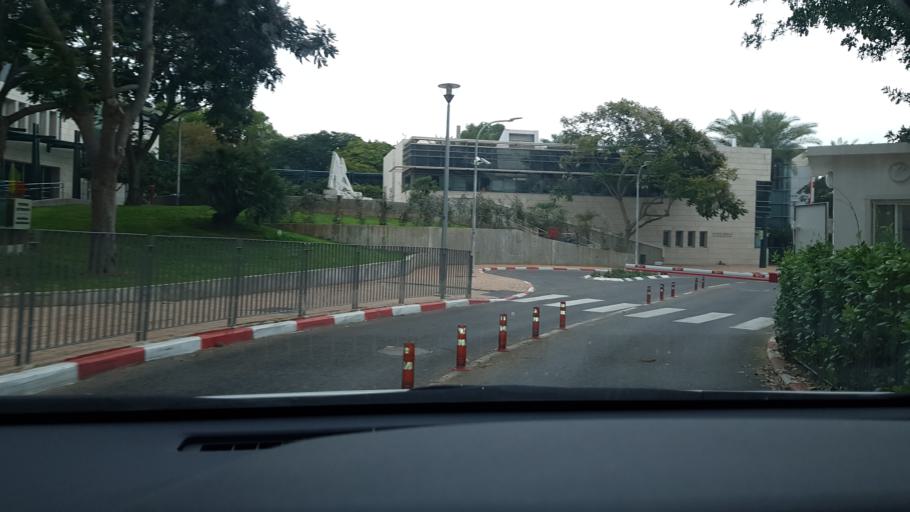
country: IL
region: Central District
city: Ness Ziona
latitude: 31.9066
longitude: 34.8202
